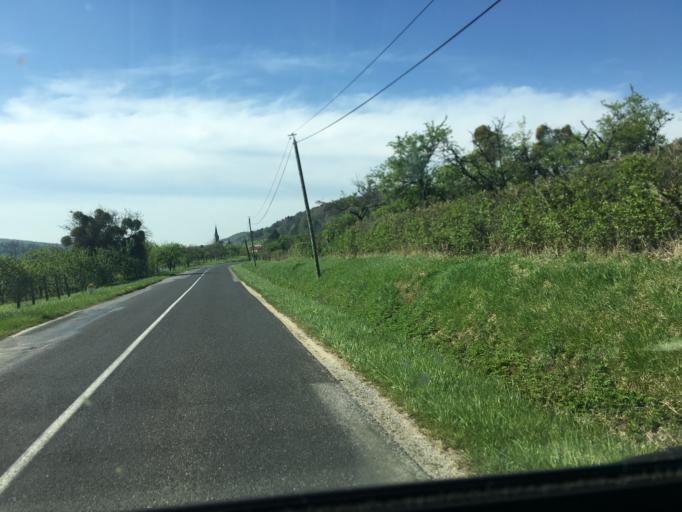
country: FR
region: Lorraine
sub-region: Departement de la Meuse
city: Vigneulles-les-Hattonchatel
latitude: 48.9019
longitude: 5.6629
